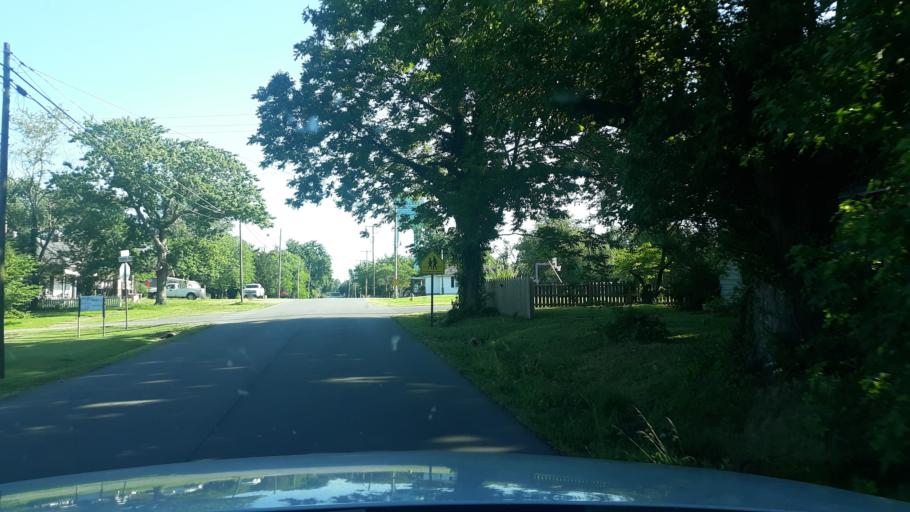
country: US
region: Illinois
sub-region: Saline County
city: Eldorado
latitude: 37.8225
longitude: -88.4363
